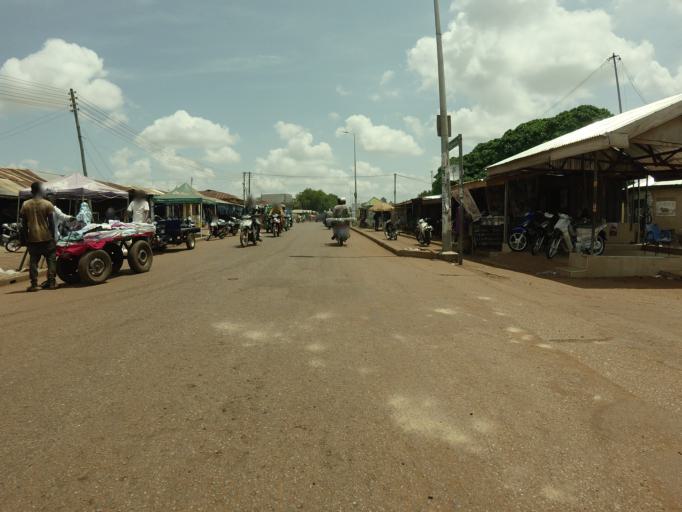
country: GH
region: Northern
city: Tamale
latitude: 9.4014
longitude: -0.8449
